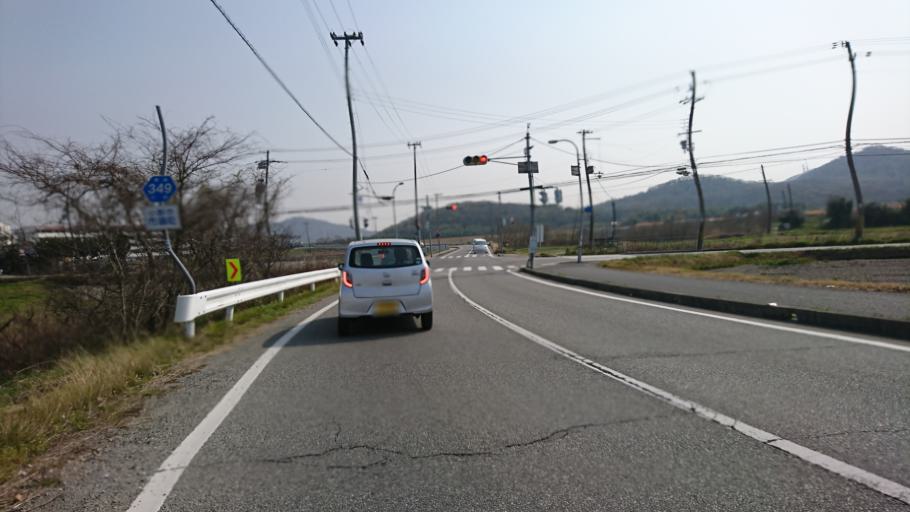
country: JP
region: Hyogo
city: Ono
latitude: 34.8297
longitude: 134.9330
